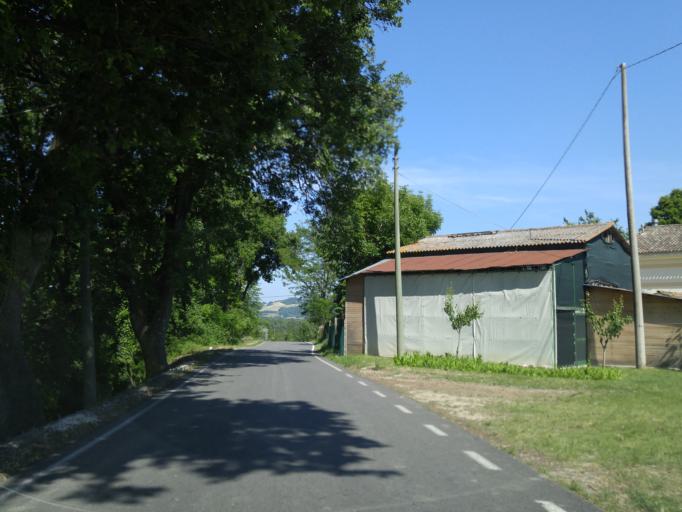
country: IT
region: The Marches
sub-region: Provincia di Pesaro e Urbino
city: Tavernelle
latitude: 43.7251
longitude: 12.8686
